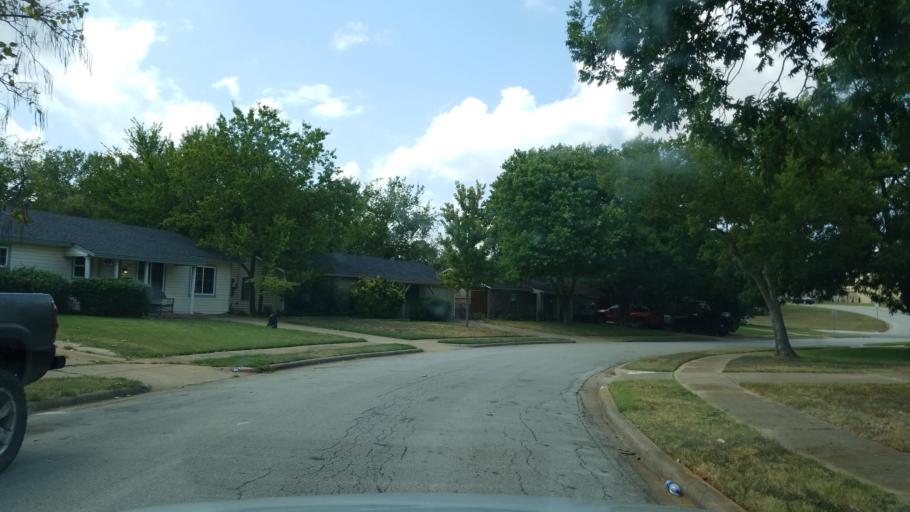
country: US
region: Texas
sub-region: Tarrant County
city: Euless
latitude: 32.8433
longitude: -97.0913
